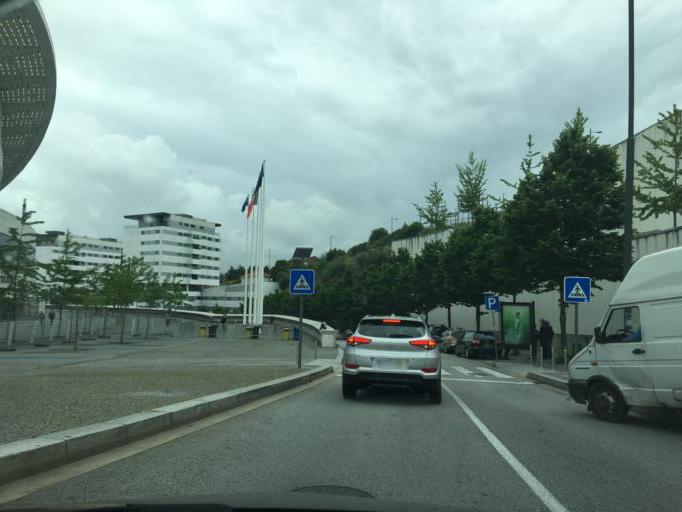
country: PT
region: Porto
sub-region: Porto
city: Porto
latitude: 41.1624
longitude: -8.5853
